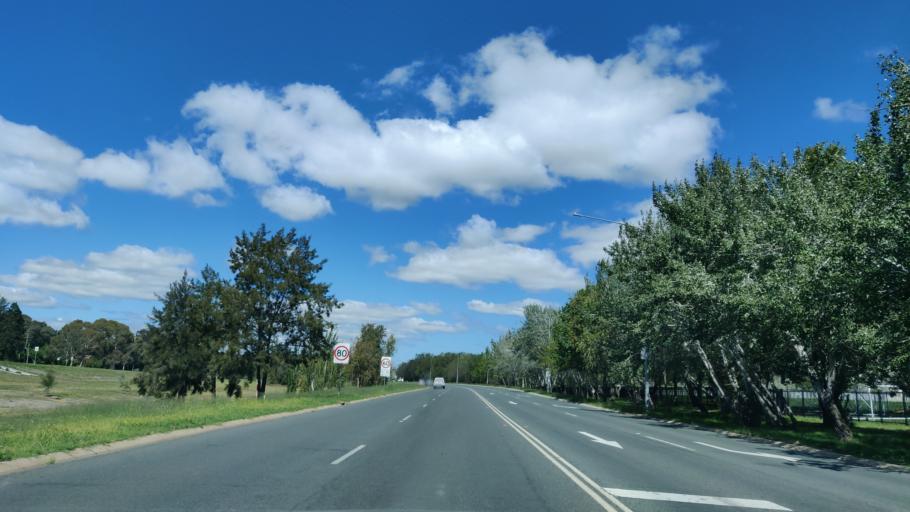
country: AU
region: Australian Capital Territory
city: Forrest
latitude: -35.3587
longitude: 149.0917
